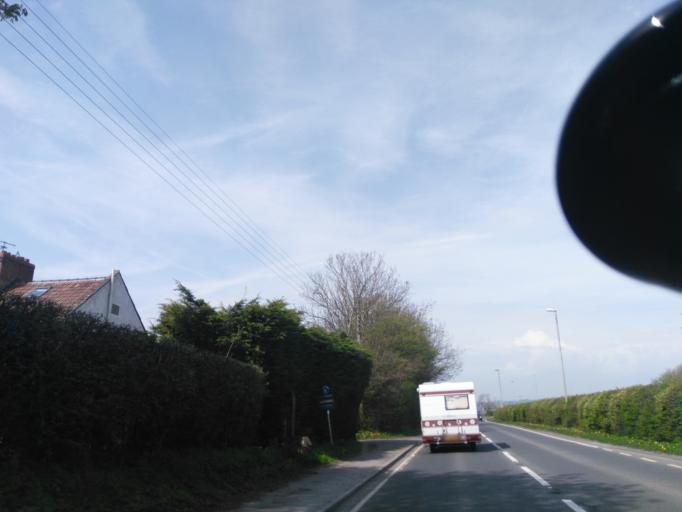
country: GB
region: England
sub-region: Somerset
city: Shepton Mallet
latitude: 51.1758
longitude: -2.5349
